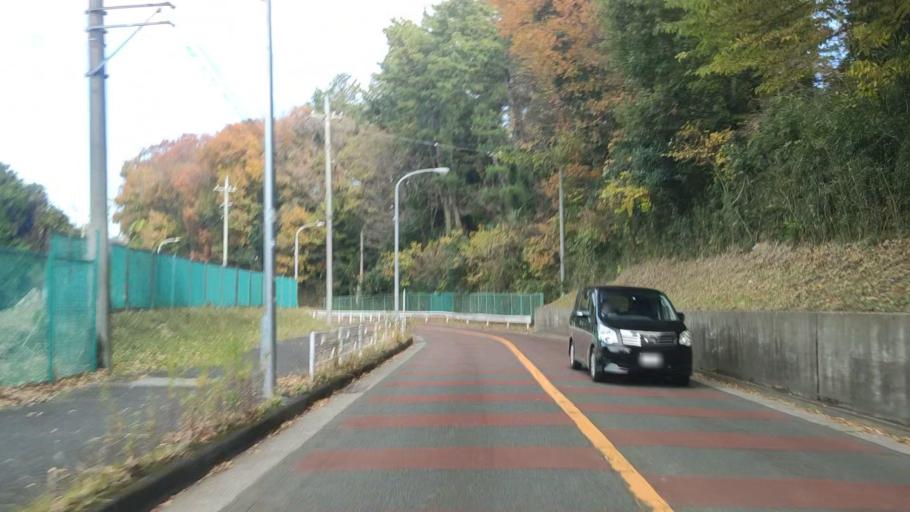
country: JP
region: Kanagawa
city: Yokohama
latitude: 35.4397
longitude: 139.5445
